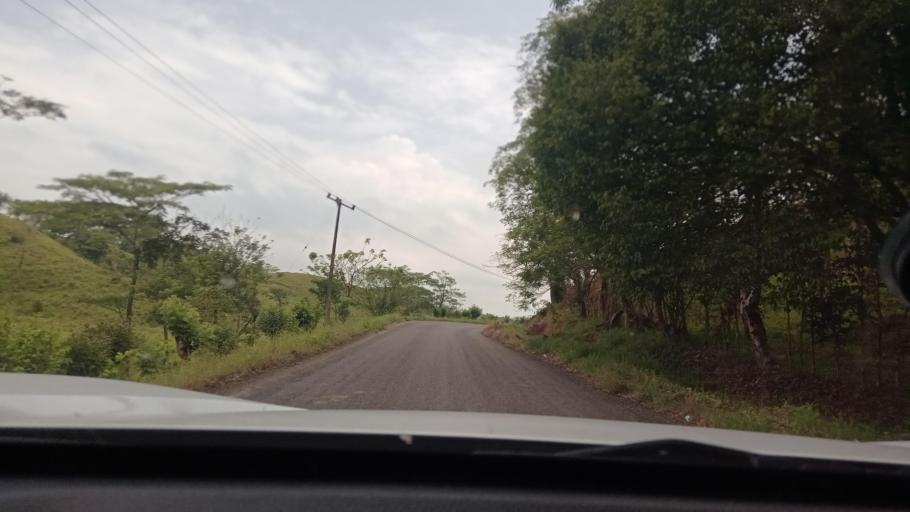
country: MX
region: Tabasco
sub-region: Huimanguillo
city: Francisco Rueda
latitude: 17.5455
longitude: -94.1288
